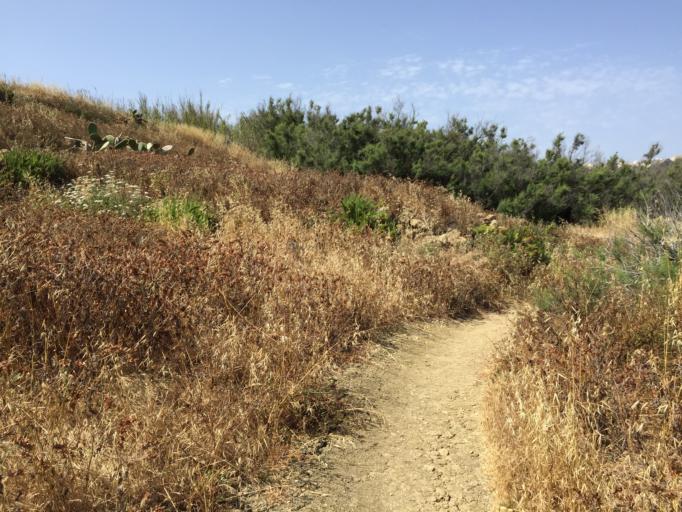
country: MT
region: In-Nadur
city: Nadur
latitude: 36.0630
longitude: 14.2876
